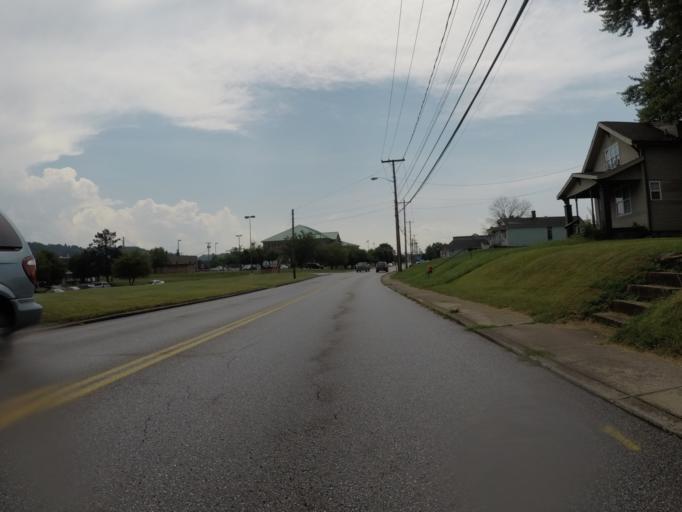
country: US
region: Kentucky
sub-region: Boyd County
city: Ashland
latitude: 38.4820
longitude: -82.6514
